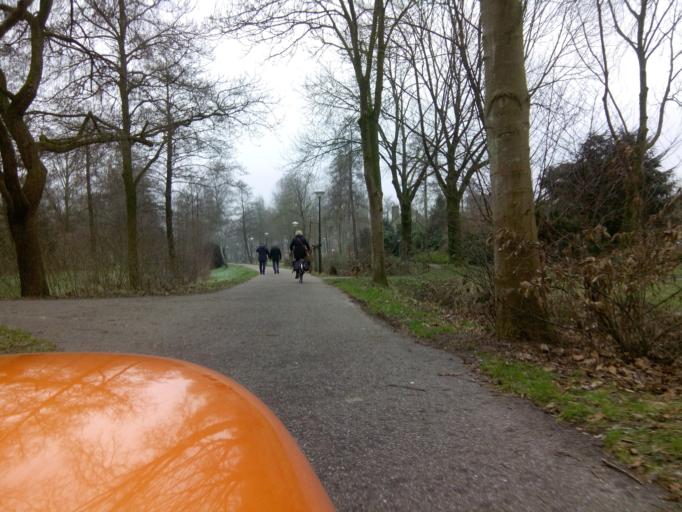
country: NL
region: Utrecht
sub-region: Gemeente Leusden
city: Leusden
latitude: 52.1298
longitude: 5.4405
